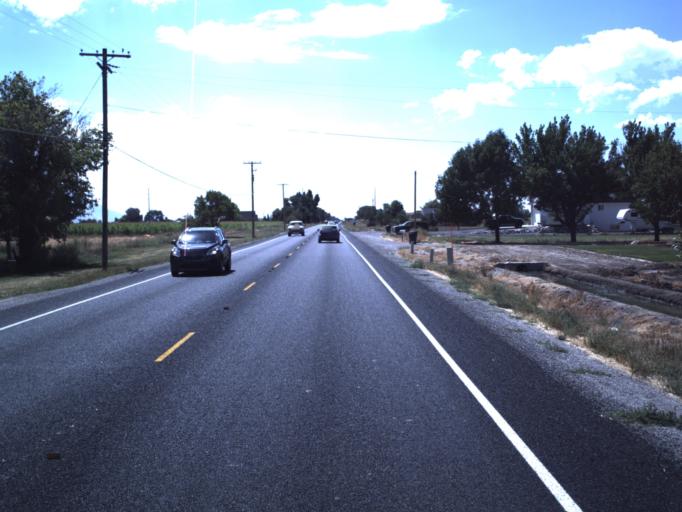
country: US
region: Utah
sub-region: Box Elder County
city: Garland
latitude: 41.7319
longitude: -112.1432
